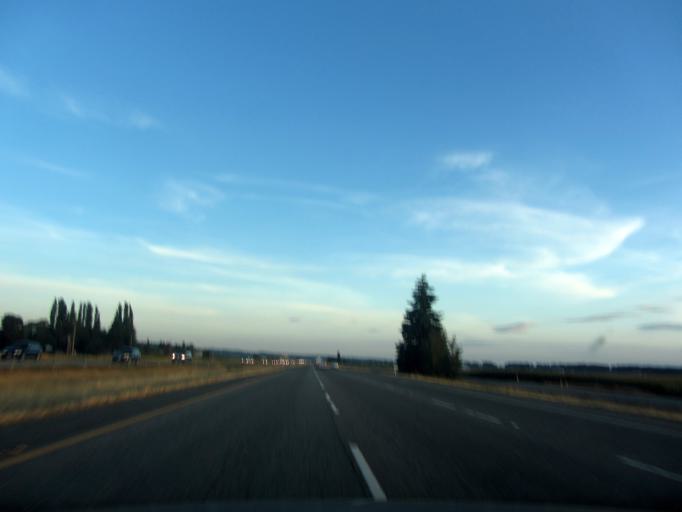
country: US
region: Washington
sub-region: Skagit County
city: Mount Vernon
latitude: 48.3726
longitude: -122.3357
